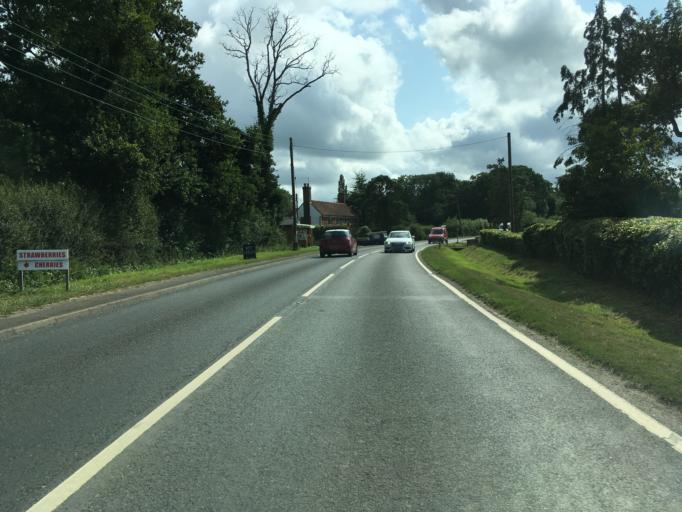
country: GB
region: England
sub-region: Kent
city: Headcorn
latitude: 51.1226
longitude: 0.6475
